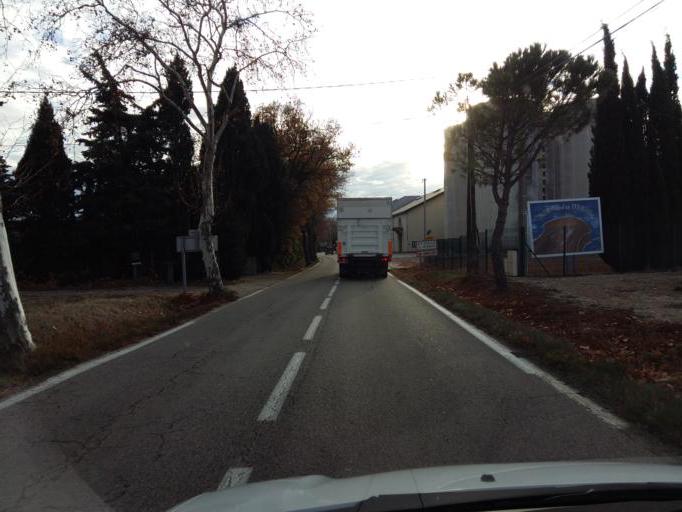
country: FR
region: Provence-Alpes-Cote d'Azur
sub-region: Departement du Vaucluse
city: Sainte-Cecile-les-Vignes
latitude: 44.2517
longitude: 4.8909
